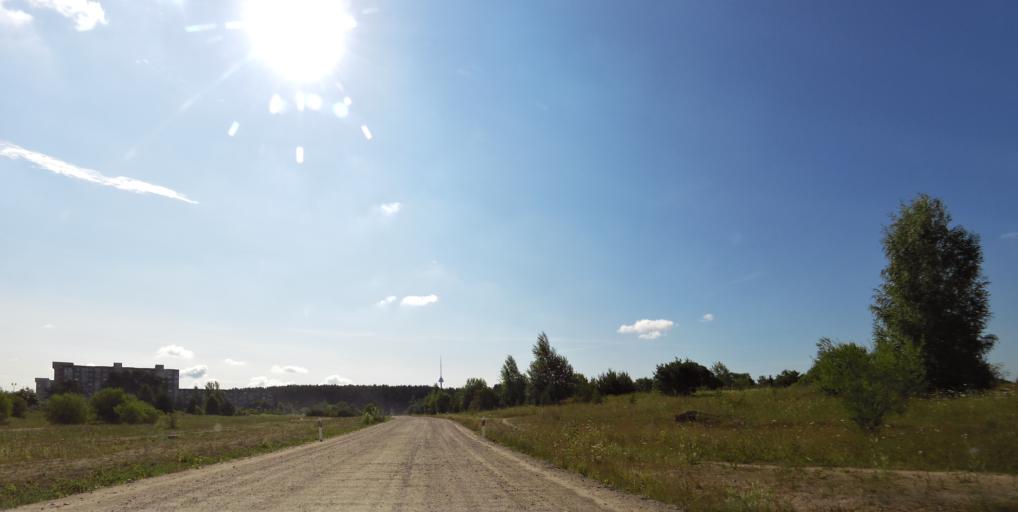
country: LT
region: Vilnius County
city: Pilaite
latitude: 54.7027
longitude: 25.1764
